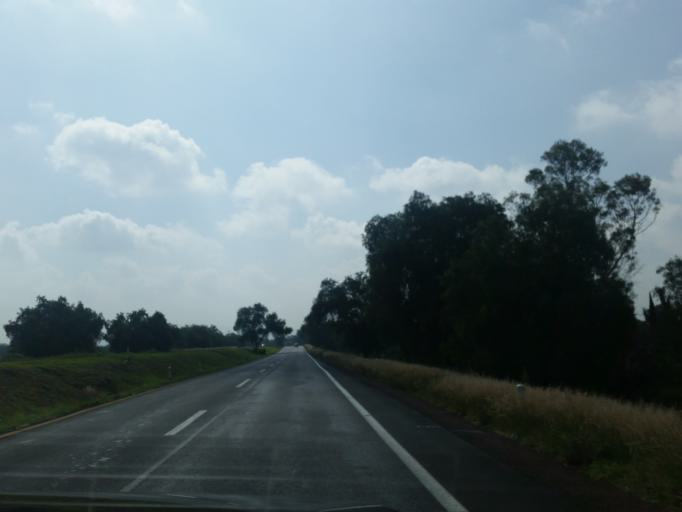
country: MX
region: Mexico
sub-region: Acolman de Nezahualcoyotl
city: Prados de San Juan
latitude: 19.6210
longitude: -98.9664
